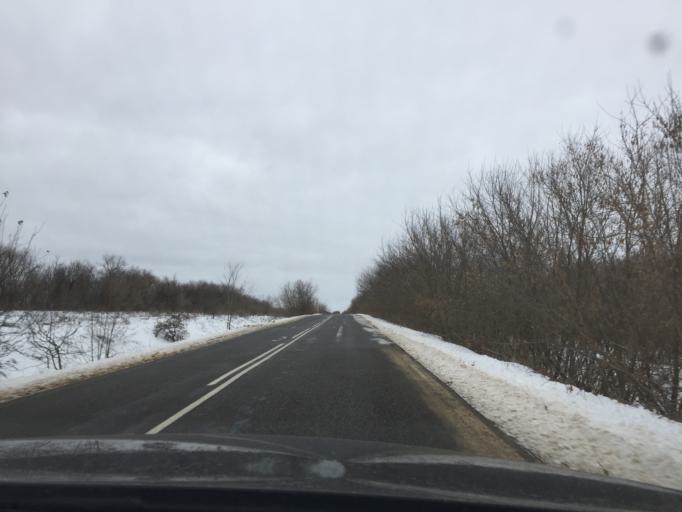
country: RU
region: Tula
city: Teploye
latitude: 53.7920
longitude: 37.6070
